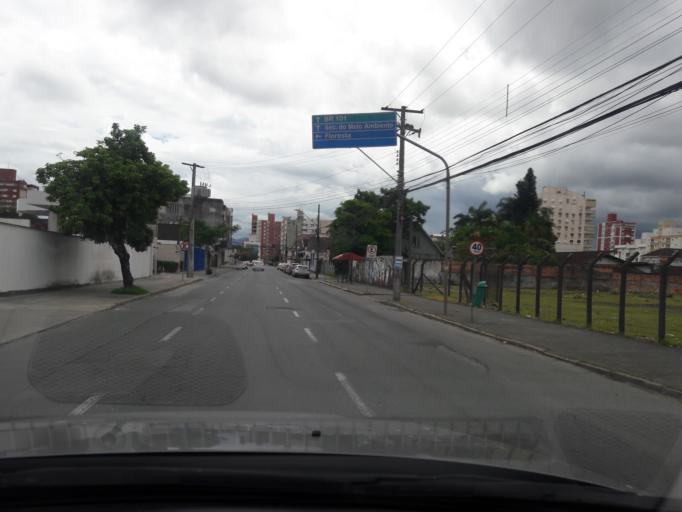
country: BR
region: Santa Catarina
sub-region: Joinville
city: Joinville
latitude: -26.3147
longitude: -48.8439
